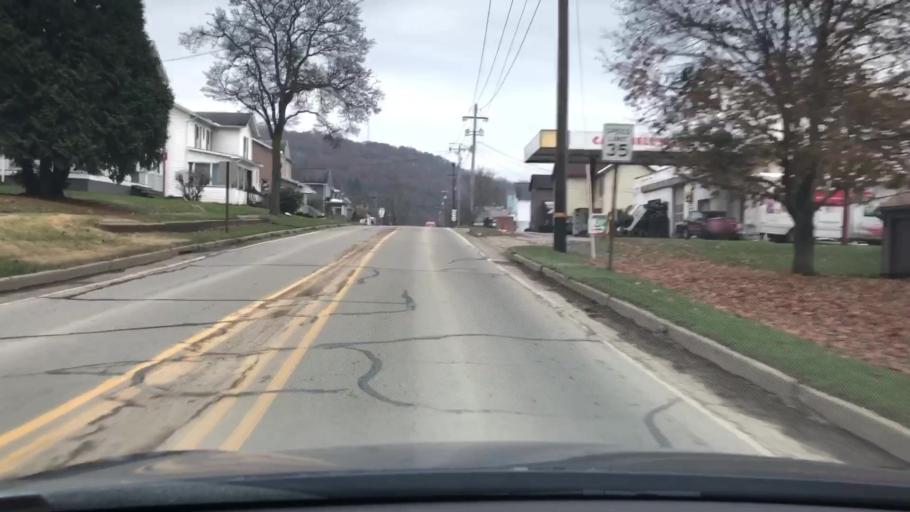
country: US
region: Pennsylvania
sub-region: Clarion County
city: Clarion
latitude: 41.0010
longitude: -79.3376
